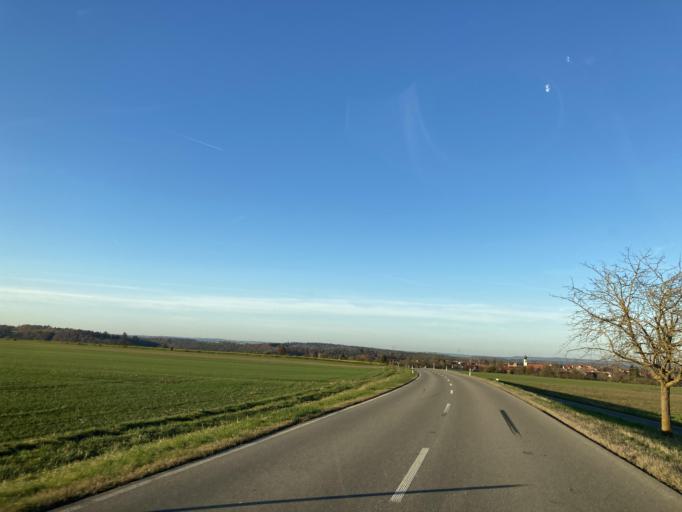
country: DE
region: Baden-Wuerttemberg
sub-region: Tuebingen Region
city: Hirrlingen
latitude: 48.4420
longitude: 8.8786
